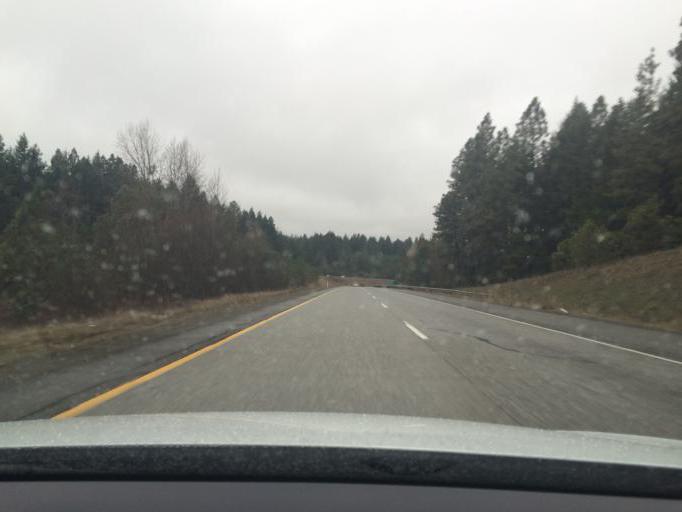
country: US
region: Washington
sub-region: Kittitas County
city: Cle Elum
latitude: 47.1619
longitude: -120.8561
